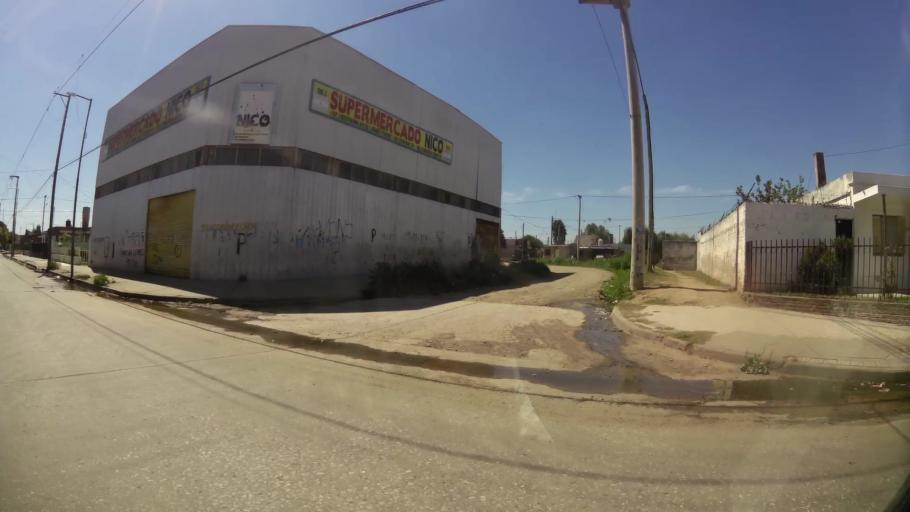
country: AR
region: Cordoba
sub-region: Departamento de Capital
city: Cordoba
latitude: -31.3673
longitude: -64.1429
